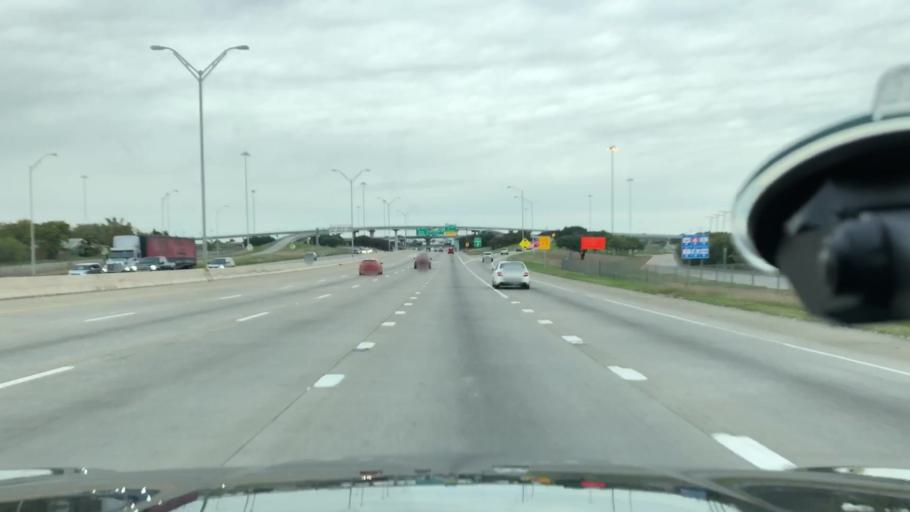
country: US
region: Texas
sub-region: Dallas County
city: DeSoto
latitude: 32.6362
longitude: -96.8231
